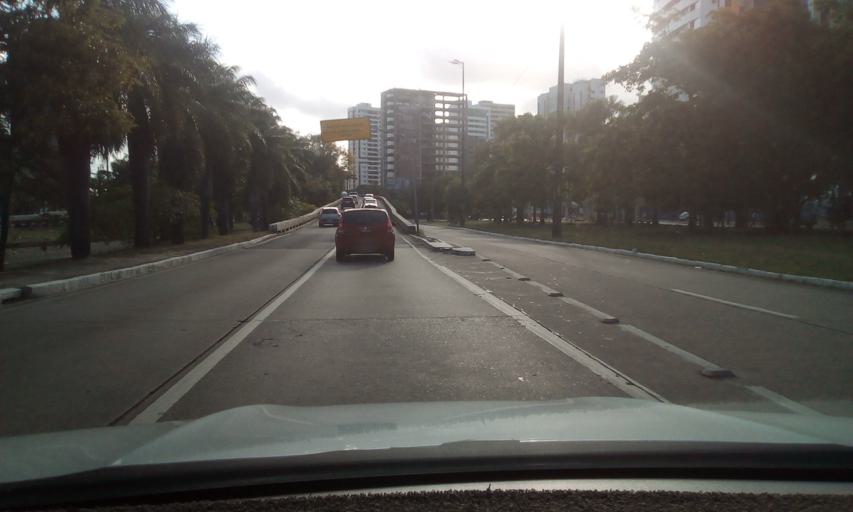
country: BR
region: Pernambuco
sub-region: Recife
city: Recife
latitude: -8.0439
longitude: -34.8882
